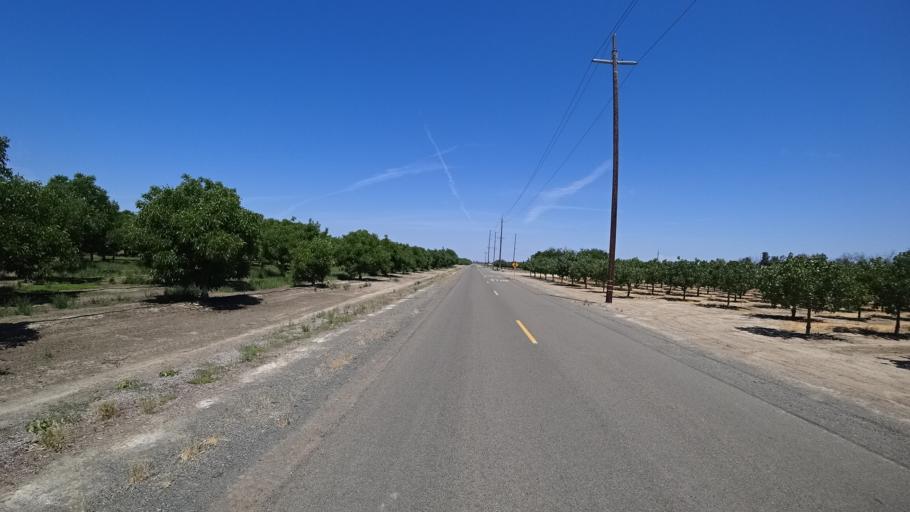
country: US
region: California
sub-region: Kings County
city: Armona
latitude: 36.2528
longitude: -119.6910
